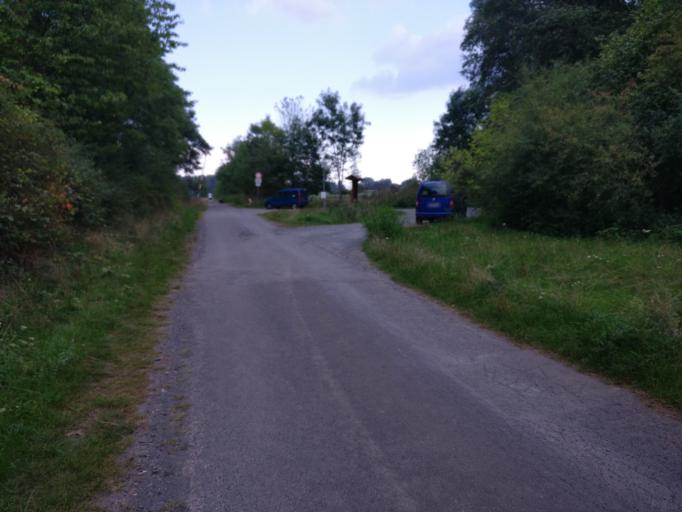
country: DE
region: Hesse
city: Solms
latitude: 50.5233
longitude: 8.4267
